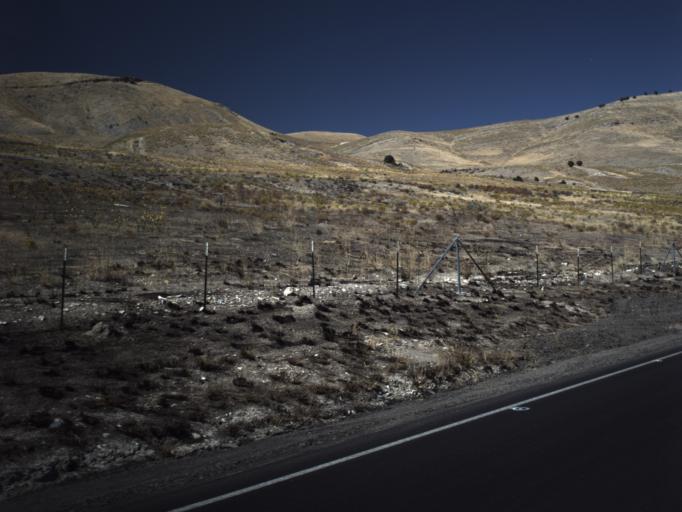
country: US
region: Utah
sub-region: Utah County
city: Saratoga Springs
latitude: 40.2337
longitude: -111.8706
